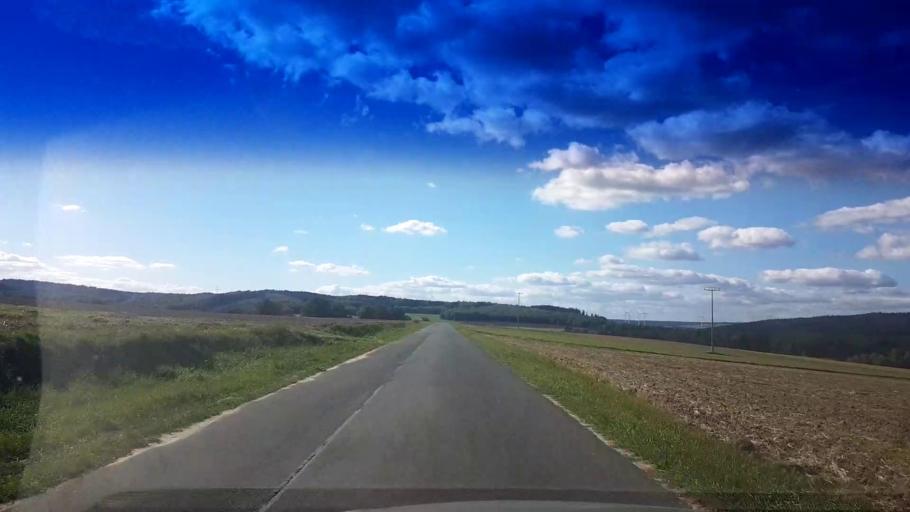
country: DE
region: Bavaria
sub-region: Upper Franconia
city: Arzberg
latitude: 50.0242
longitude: 12.2253
